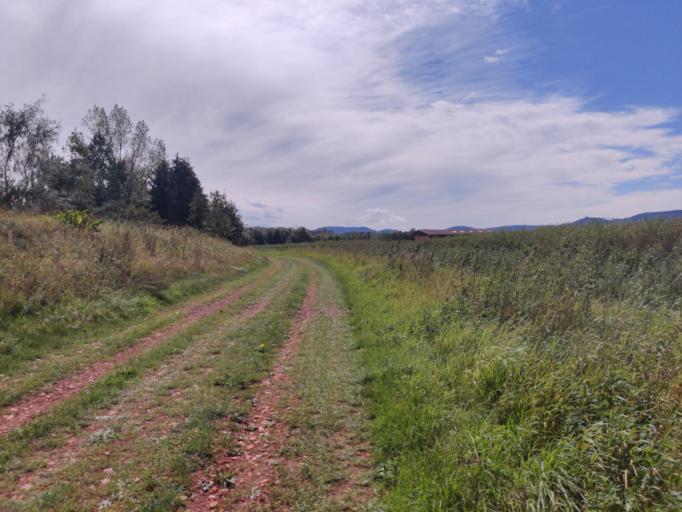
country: DE
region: Lower Saxony
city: Langelsheim
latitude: 51.9735
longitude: 10.3698
